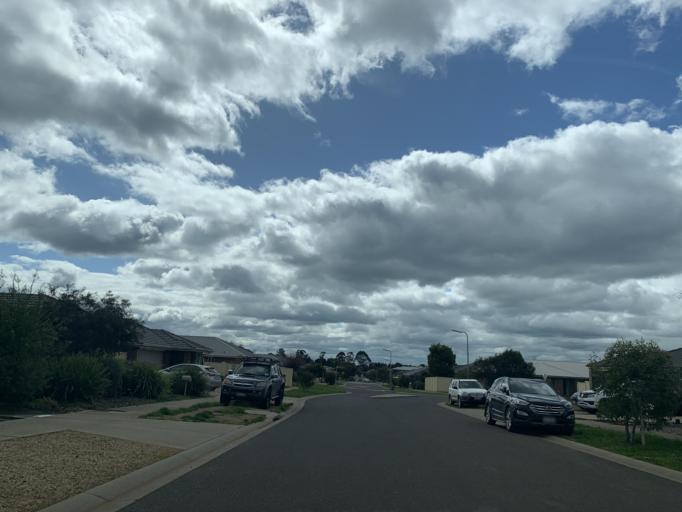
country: AU
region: Victoria
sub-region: Whittlesea
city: Whittlesea
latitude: -37.2918
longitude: 144.9355
